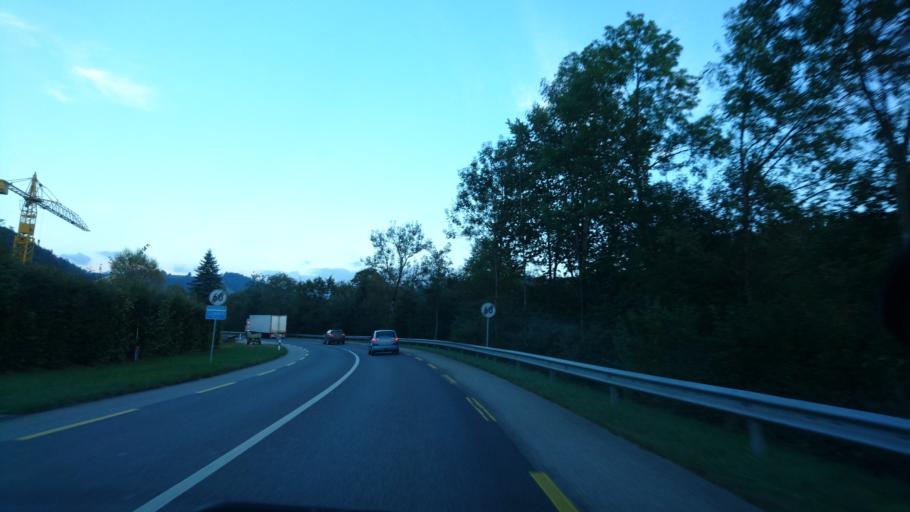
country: CH
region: Bern
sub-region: Emmental District
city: Trubschachen
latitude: 46.9234
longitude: 7.8222
